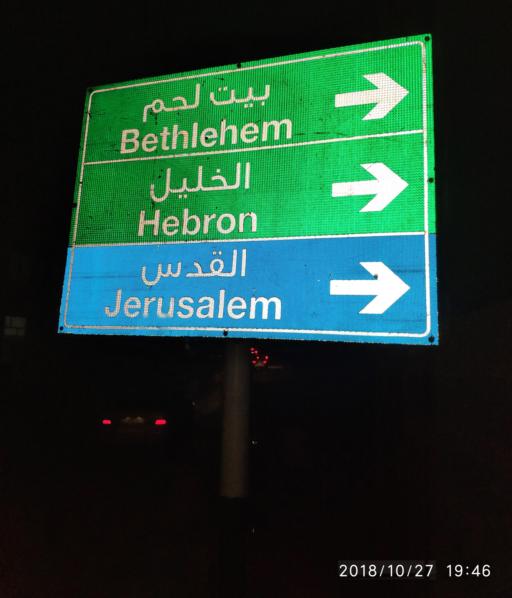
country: PS
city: Khallat Hamamah
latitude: 31.7154
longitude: 35.1968
